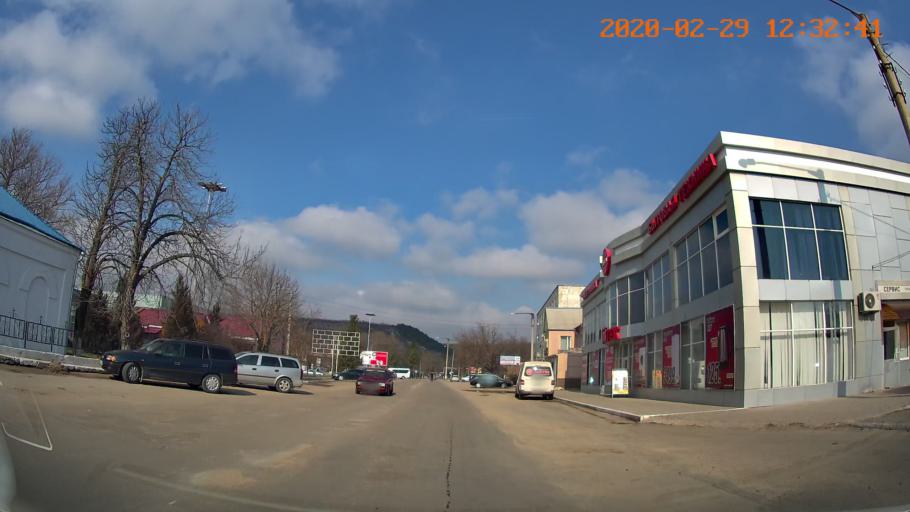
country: MD
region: Telenesti
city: Camenca
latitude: 48.0300
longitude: 28.7031
